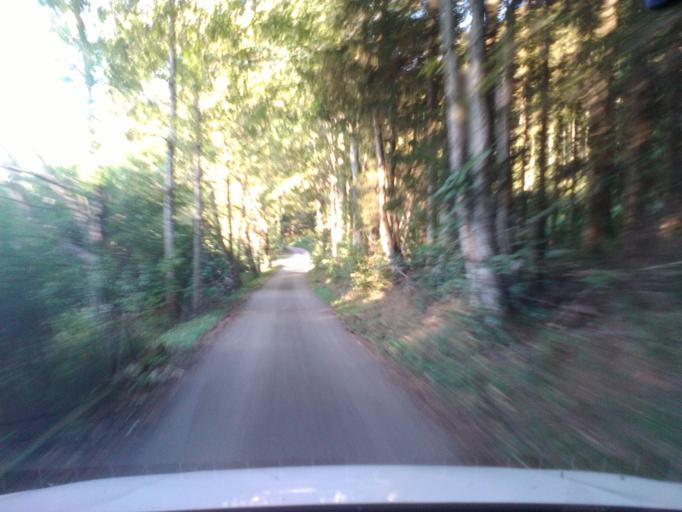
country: FR
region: Lorraine
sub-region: Departement des Vosges
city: Senones
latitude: 48.3431
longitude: 7.0561
